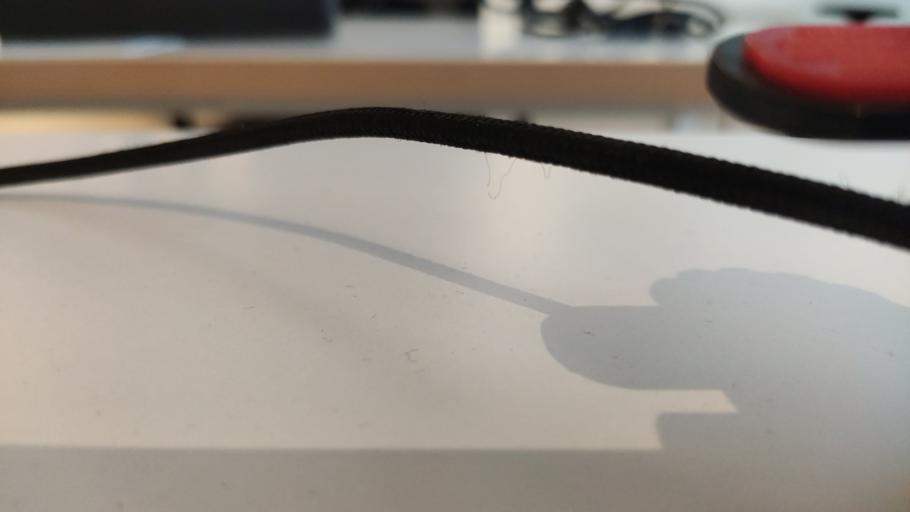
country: RU
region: Moskovskaya
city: Novopetrovskoye
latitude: 55.9361
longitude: 36.4349
